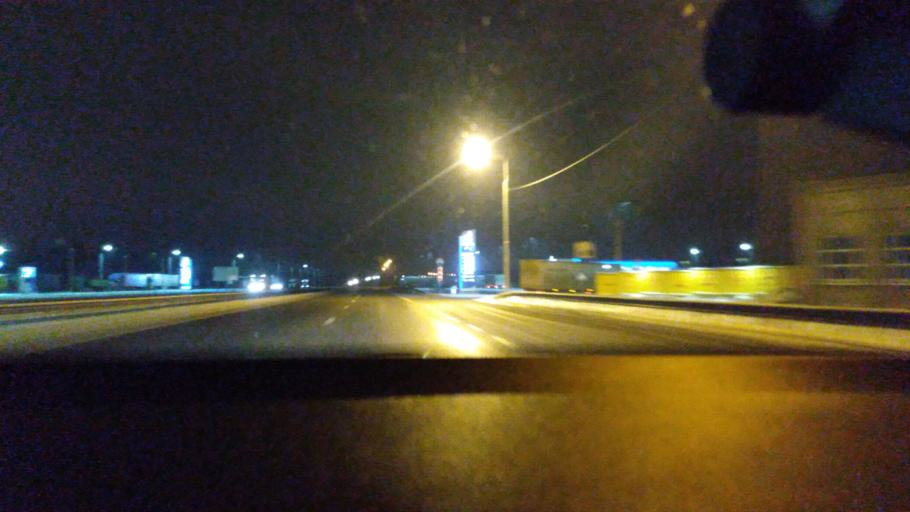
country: RU
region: Moskovskaya
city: Kolomna
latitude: 55.1227
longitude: 38.8106
